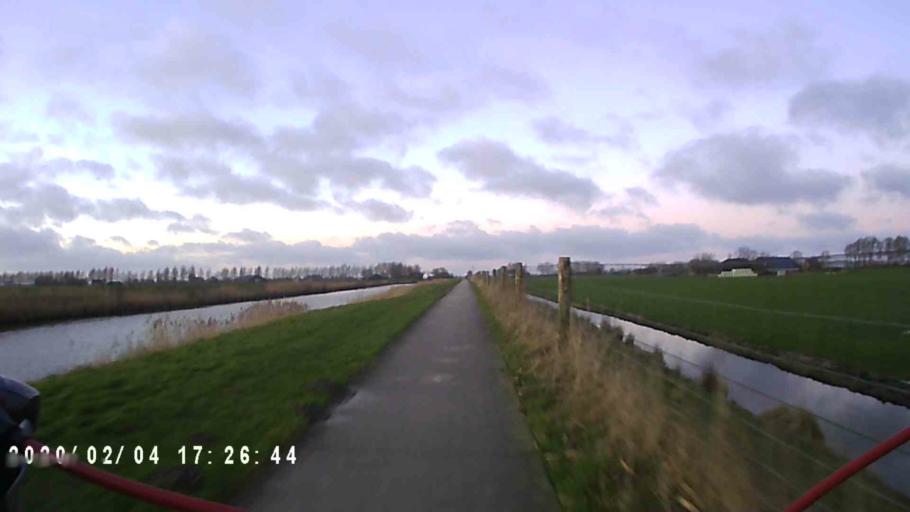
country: NL
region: Groningen
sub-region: Gemeente Zuidhorn
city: Aduard
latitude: 53.2628
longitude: 6.5085
